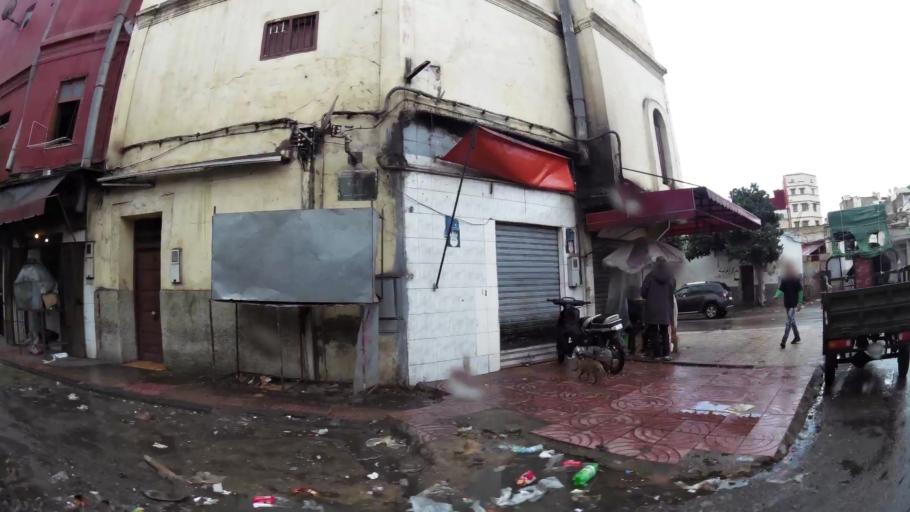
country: MA
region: Grand Casablanca
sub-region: Casablanca
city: Casablanca
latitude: 33.5732
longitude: -7.6036
